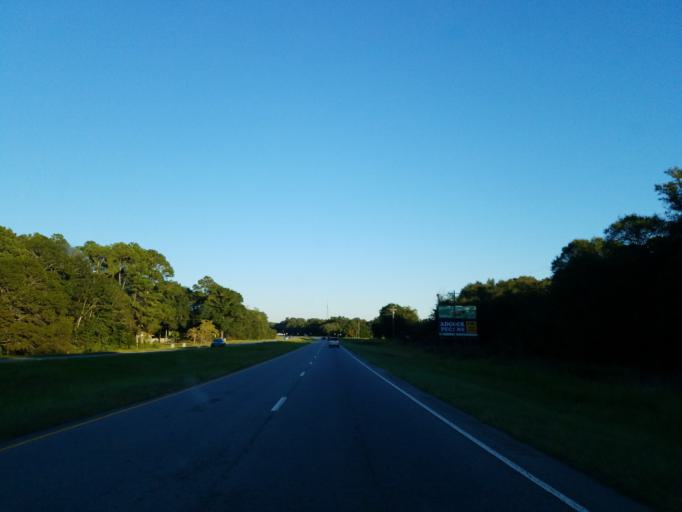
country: US
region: Georgia
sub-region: Tift County
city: Omega
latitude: 31.4760
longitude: -83.6727
